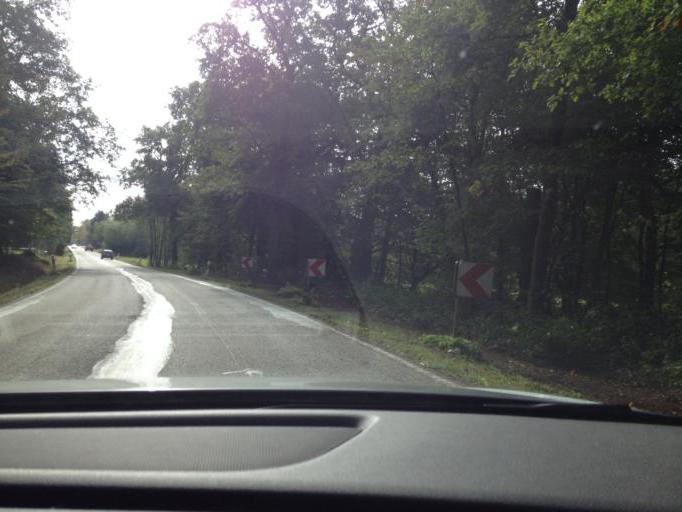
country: DE
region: Saarland
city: Mainzweiler
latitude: 49.3969
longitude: 7.1095
